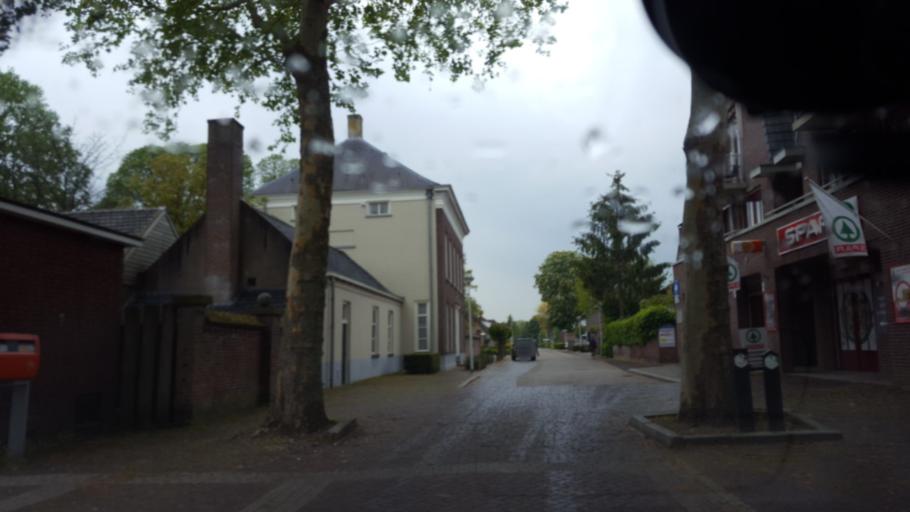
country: NL
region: North Brabant
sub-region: Gemeente Someren
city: Someren
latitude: 51.4197
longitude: 5.6819
